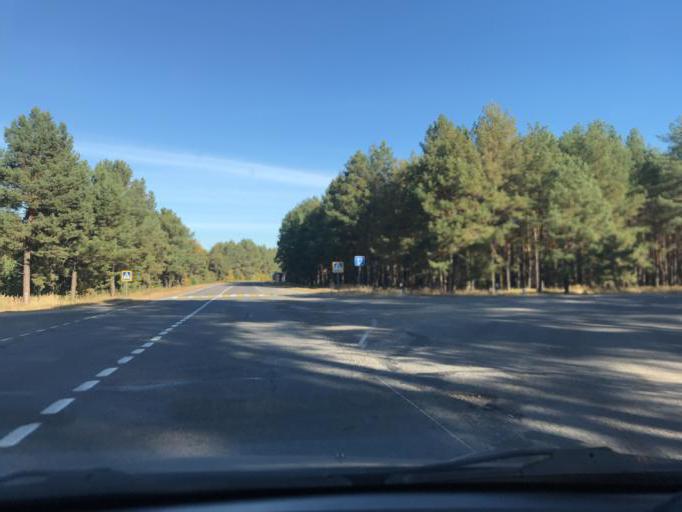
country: UA
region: Chernihiv
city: Lyubech
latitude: 51.6047
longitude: 30.4709
